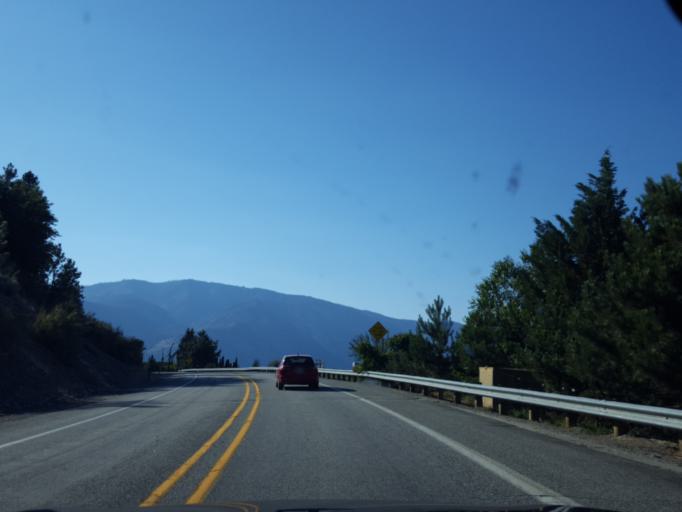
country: US
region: Washington
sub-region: Chelan County
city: Manson
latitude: 47.8591
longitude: -120.1488
